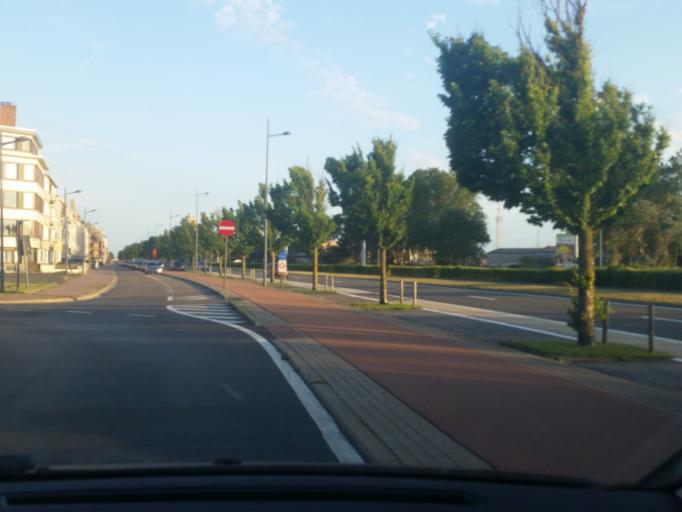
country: BE
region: Flanders
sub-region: Provincie West-Vlaanderen
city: Ostend
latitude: 51.2367
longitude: 2.9403
